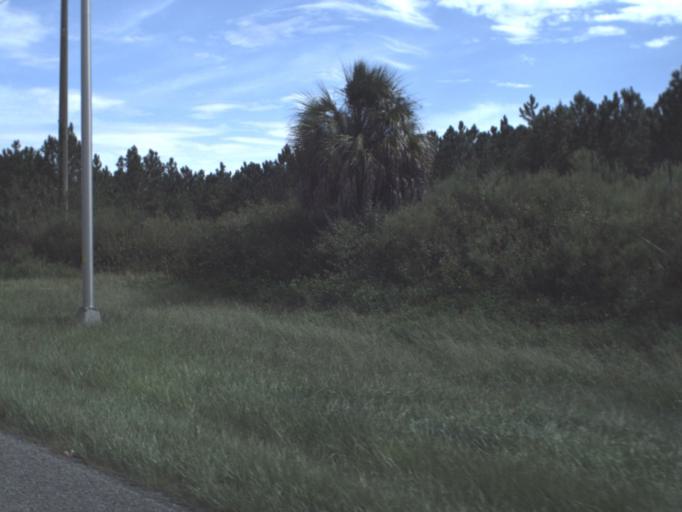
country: US
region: Florida
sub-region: Polk County
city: Fuller Heights
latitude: 27.9034
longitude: -82.0074
